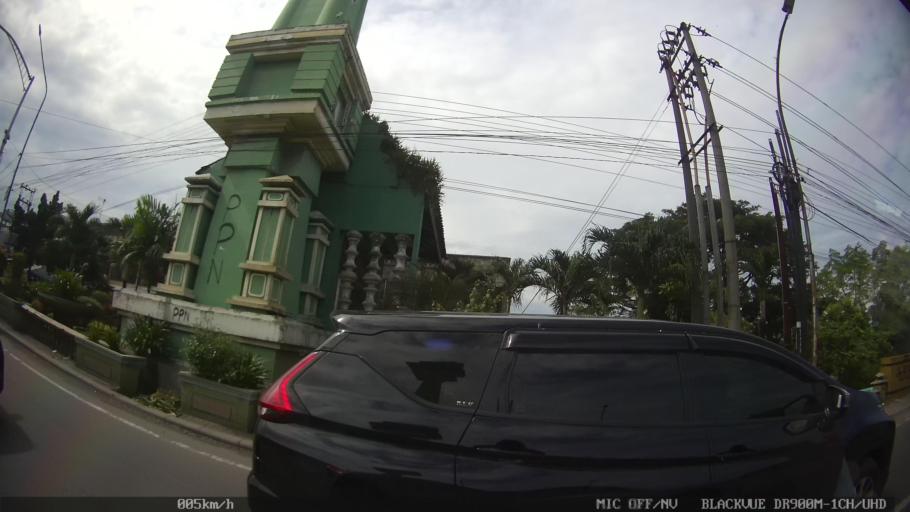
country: ID
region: North Sumatra
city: Sunggal
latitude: 3.5987
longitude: 98.6061
